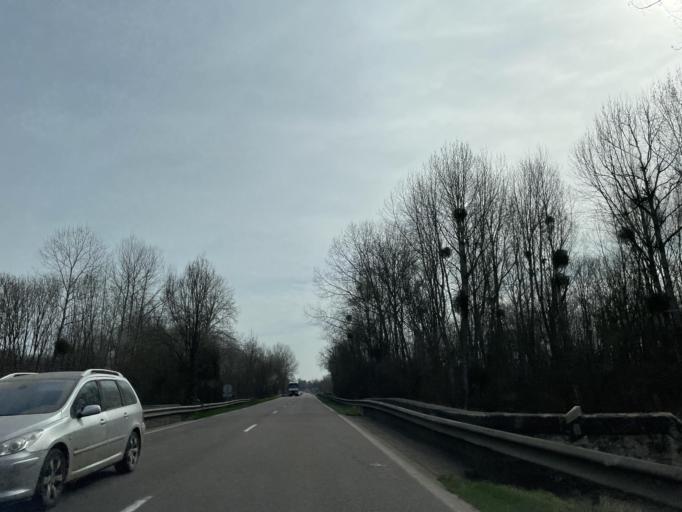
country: FR
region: Champagne-Ardenne
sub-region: Departement de l'Aube
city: Nogent-sur-Seine
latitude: 48.5033
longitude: 3.4565
